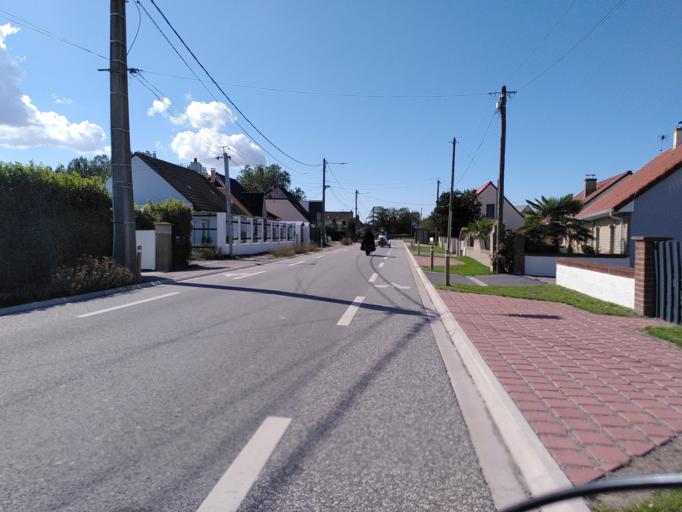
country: FR
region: Nord-Pas-de-Calais
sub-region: Departement du Pas-de-Calais
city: Oye-Plage
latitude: 50.9874
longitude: 2.0419
